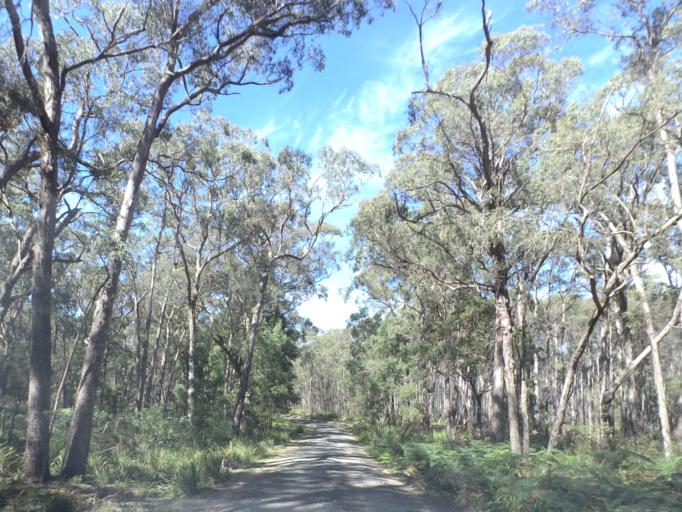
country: AU
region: Victoria
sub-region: Moorabool
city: Bacchus Marsh
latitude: -37.4110
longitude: 144.3292
